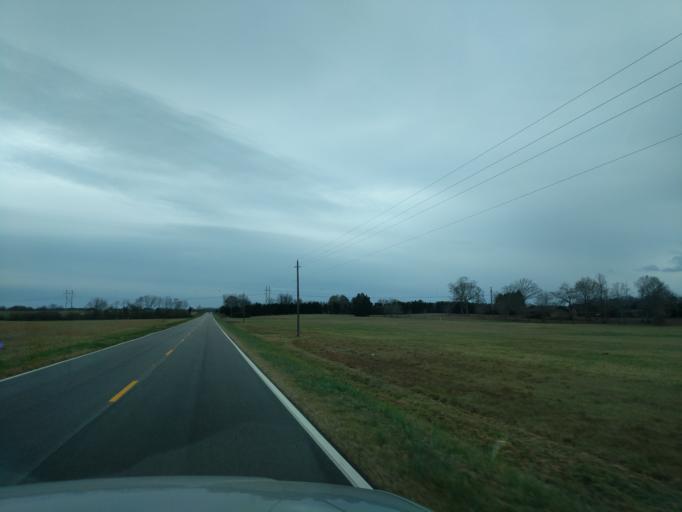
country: US
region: South Carolina
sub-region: Laurens County
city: Laurens
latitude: 34.3640
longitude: -81.9923
